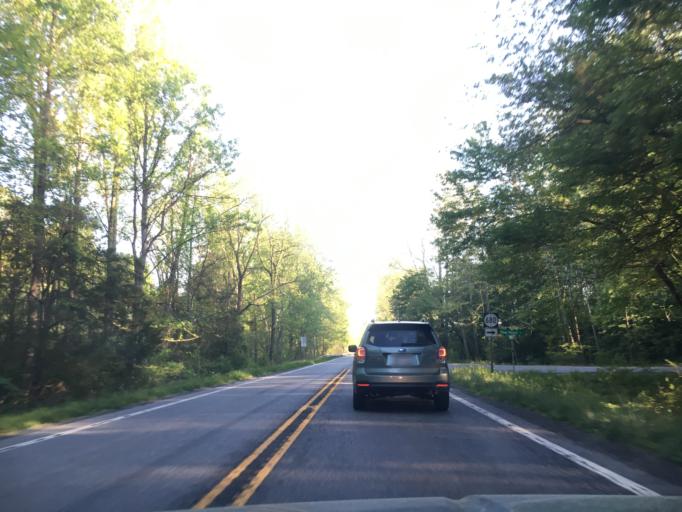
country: US
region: Virginia
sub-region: Campbell County
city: Rustburg
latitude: 37.2956
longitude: -79.1098
